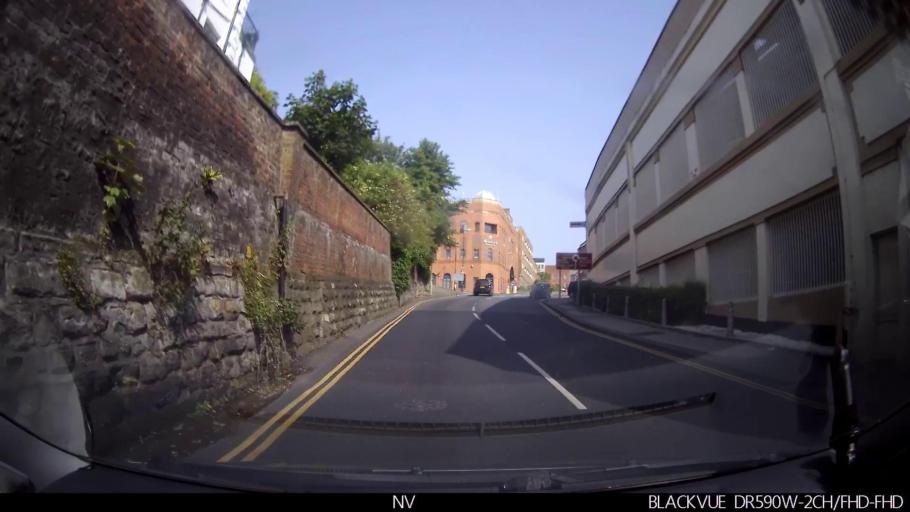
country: GB
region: England
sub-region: North Yorkshire
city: Scarborough
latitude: 54.2802
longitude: -0.4004
